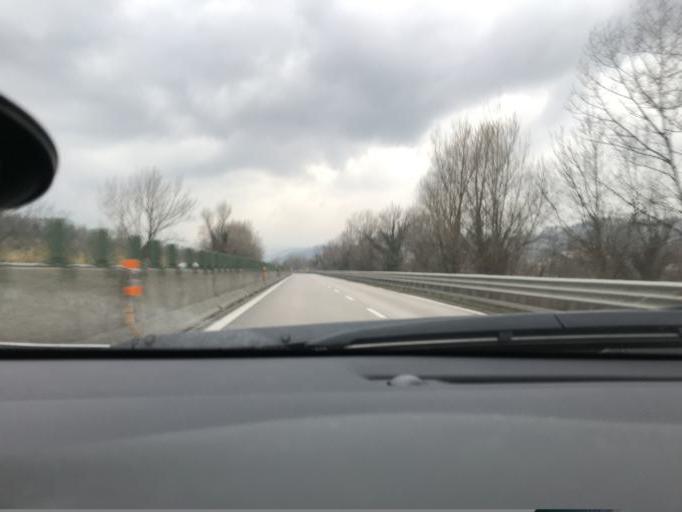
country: IT
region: The Marches
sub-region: Provincia di Ancona
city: Maiolati Spontini
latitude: 43.4932
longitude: 13.1089
